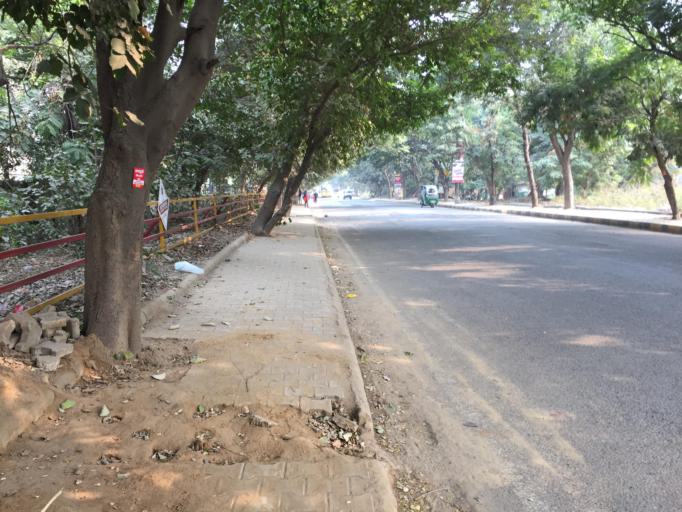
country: IN
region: Haryana
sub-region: Gurgaon
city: Gurgaon
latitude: 28.4247
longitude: 77.0963
